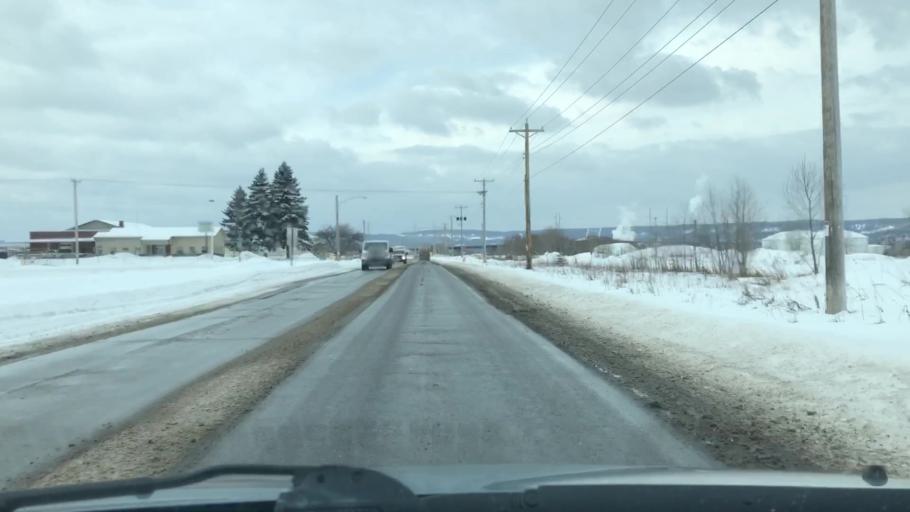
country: US
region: Wisconsin
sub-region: Douglas County
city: Superior
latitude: 46.7280
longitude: -92.1194
